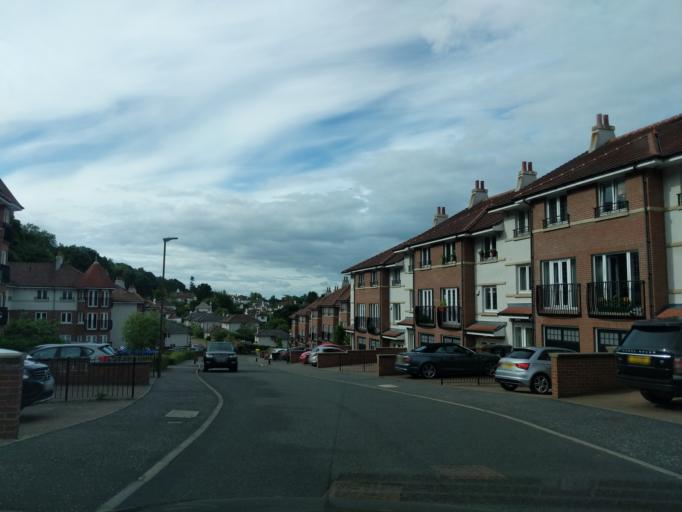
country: GB
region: Scotland
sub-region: Edinburgh
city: Colinton
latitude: 55.9574
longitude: -3.2712
